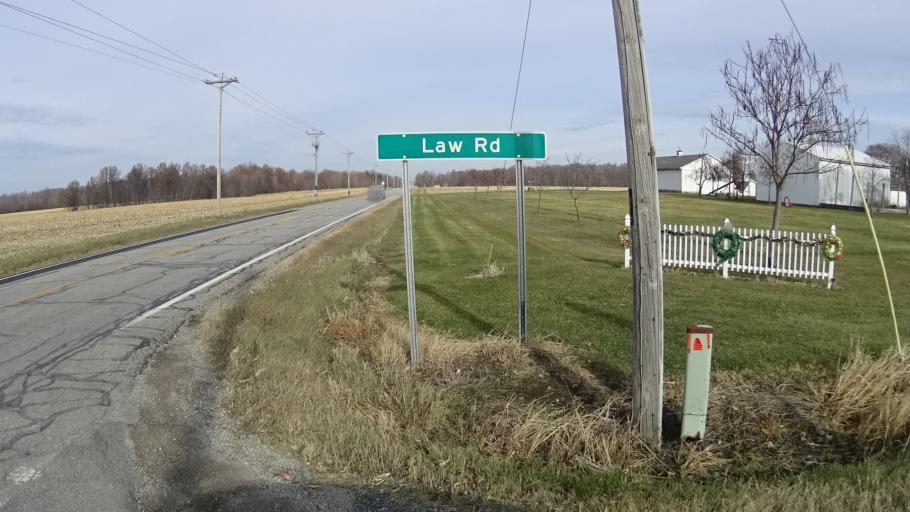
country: US
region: Ohio
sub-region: Lorain County
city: Grafton
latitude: 41.2224
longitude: -81.9835
